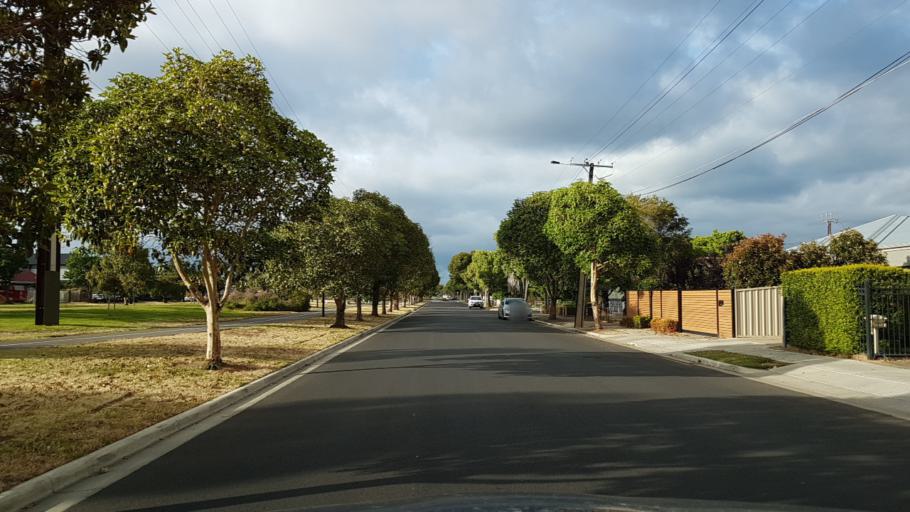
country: AU
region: South Australia
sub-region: City of West Torrens
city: Plympton
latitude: -34.9527
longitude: 138.5600
